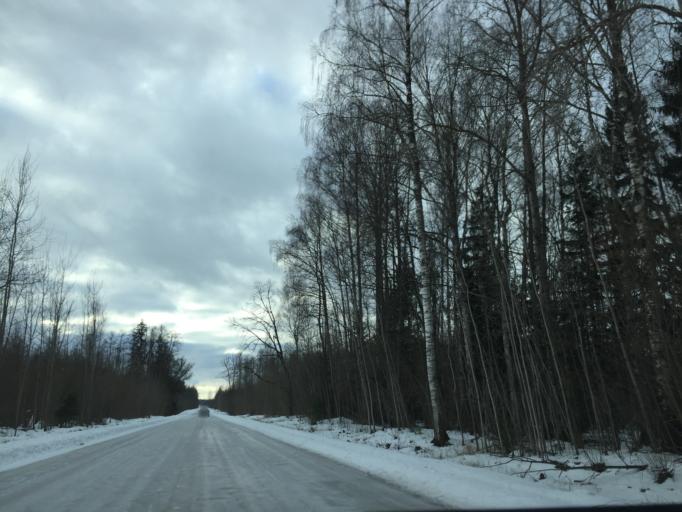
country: LV
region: Lielvarde
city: Lielvarde
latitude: 56.5985
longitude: 24.7413
